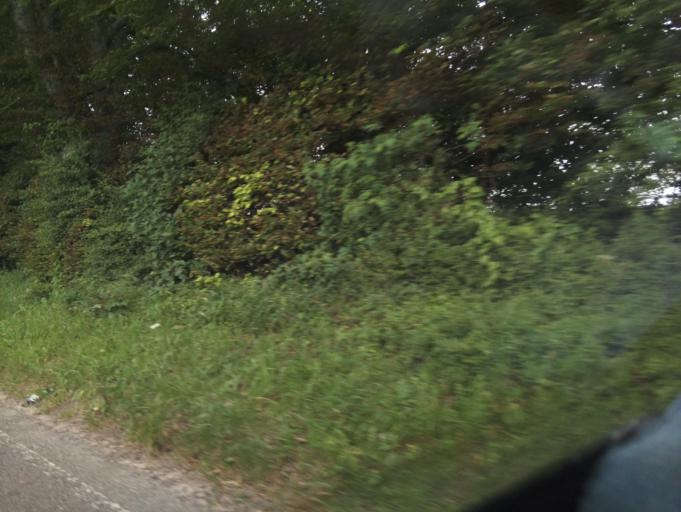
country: GB
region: England
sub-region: Dorset
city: Sherborne
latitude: 50.9649
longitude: -2.5153
